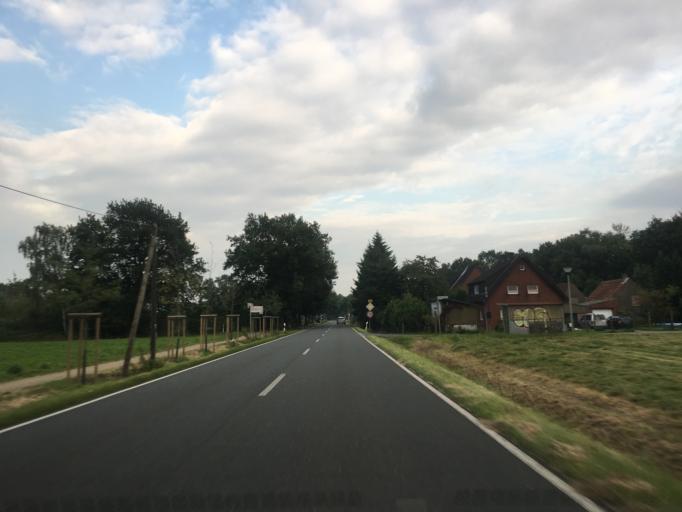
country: DE
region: North Rhine-Westphalia
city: Selm
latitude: 51.7088
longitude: 7.4385
